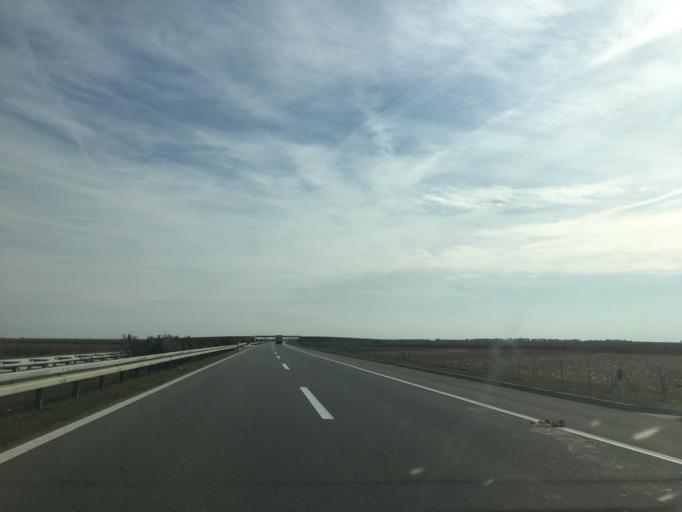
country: RS
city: Novi Karlovci
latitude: 45.0528
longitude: 20.1714
